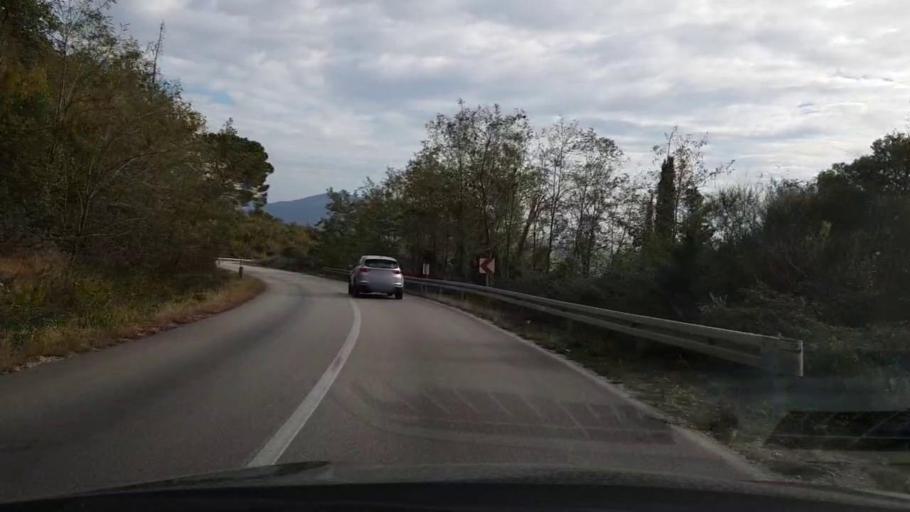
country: ME
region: Herceg Novi
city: Herceg-Novi
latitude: 42.4723
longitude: 18.5353
